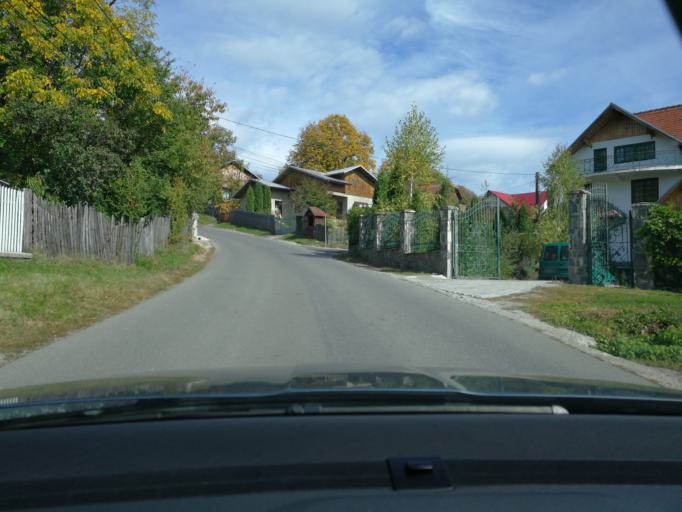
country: RO
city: Brebu Manastirei
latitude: 45.1852
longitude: 25.7656
